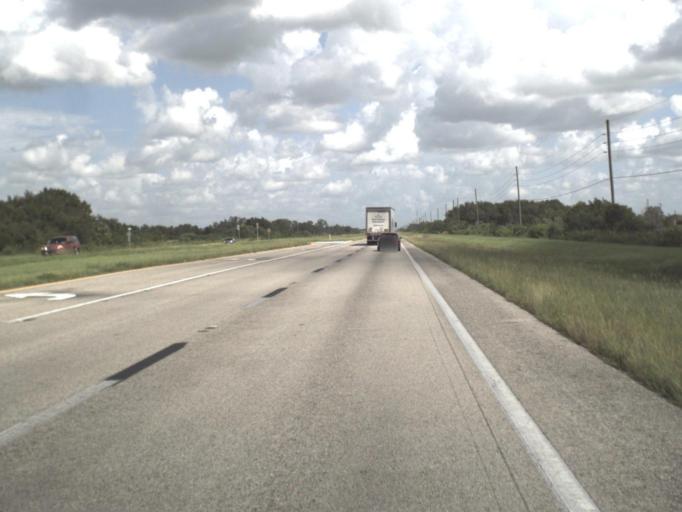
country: US
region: Florida
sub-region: Charlotte County
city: Harbour Heights
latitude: 27.0100
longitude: -81.9585
